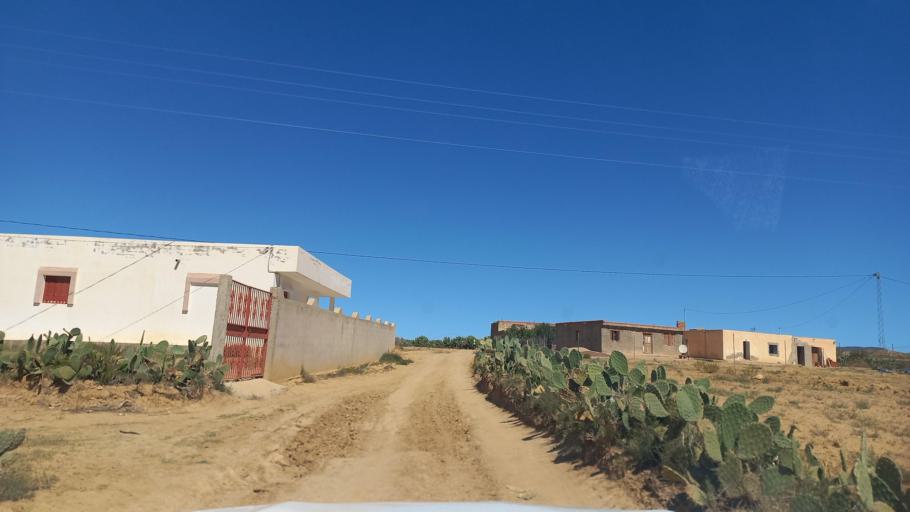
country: TN
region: Al Qasrayn
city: Sbiba
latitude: 35.3500
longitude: 9.1015
